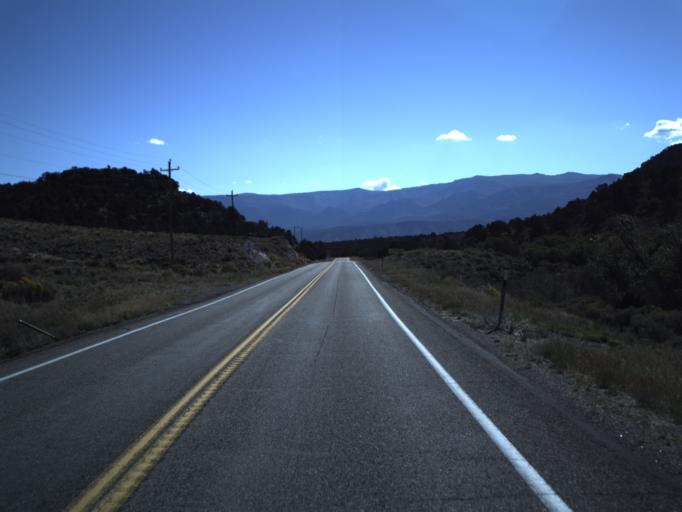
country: US
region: Utah
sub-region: Iron County
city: Cedar City
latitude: 37.6370
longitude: -113.2808
